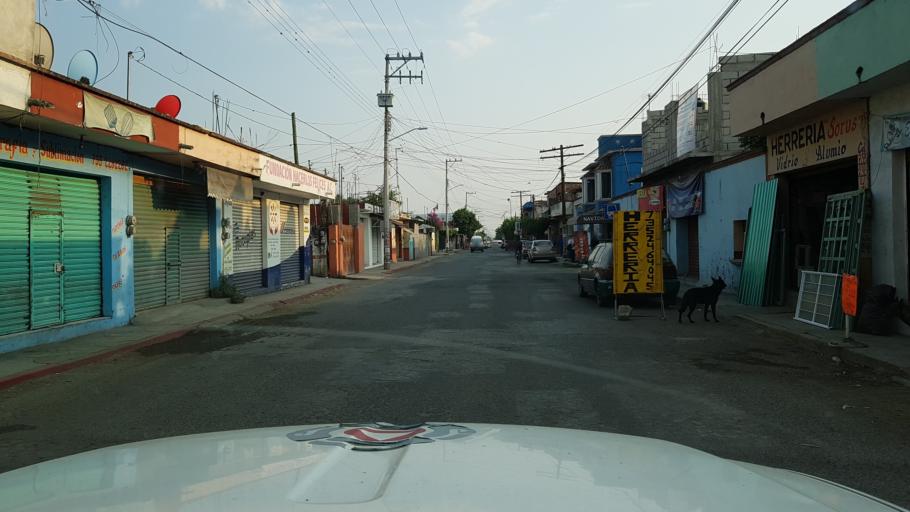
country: MX
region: Morelos
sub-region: Ayala
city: Ciudad Ayala
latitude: 18.7804
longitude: -98.9806
